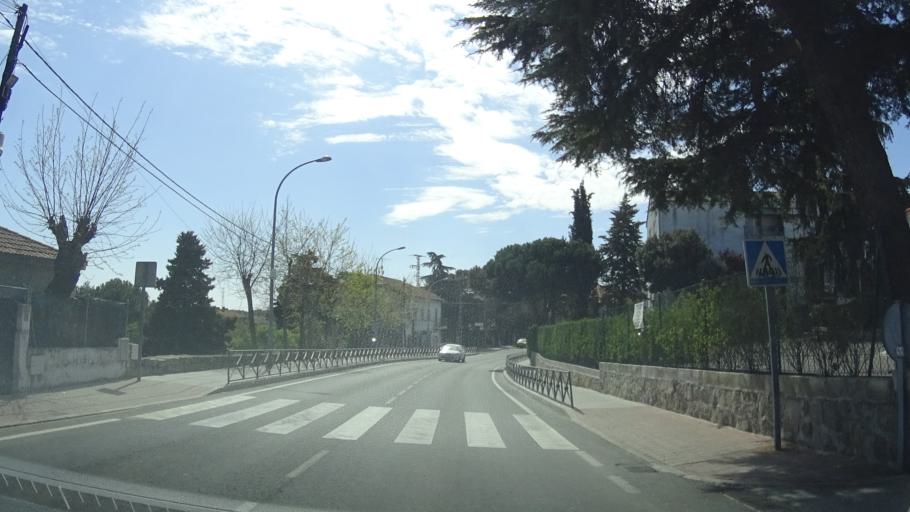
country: ES
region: Madrid
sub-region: Provincia de Madrid
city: Hoyo de Manzanares
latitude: 40.6218
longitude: -3.9042
